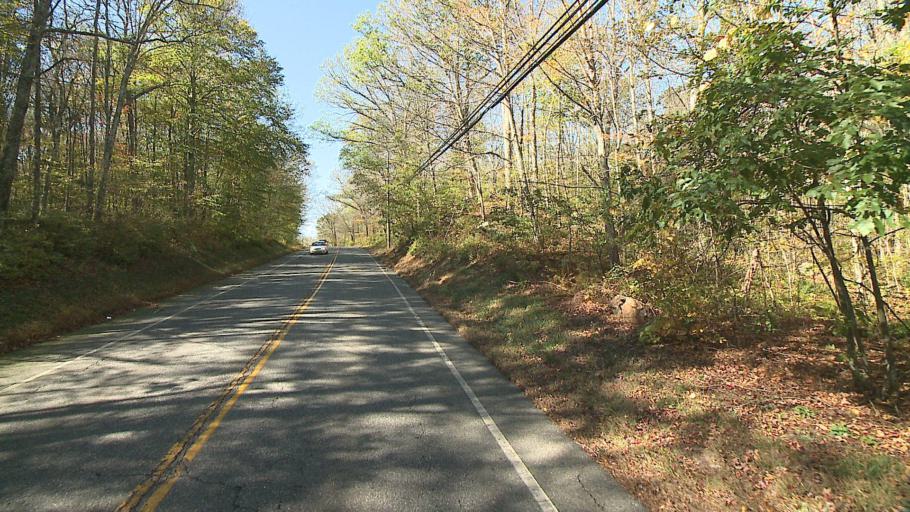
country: US
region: Connecticut
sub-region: Hartford County
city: Terramuggus
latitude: 41.6482
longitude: -72.4252
